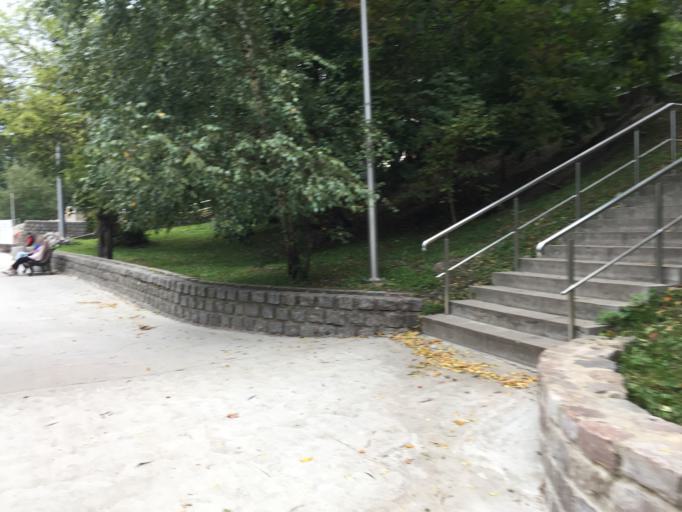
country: RU
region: Kaliningrad
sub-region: Gorod Kaliningrad
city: Kaliningrad
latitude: 54.7172
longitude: 20.5204
